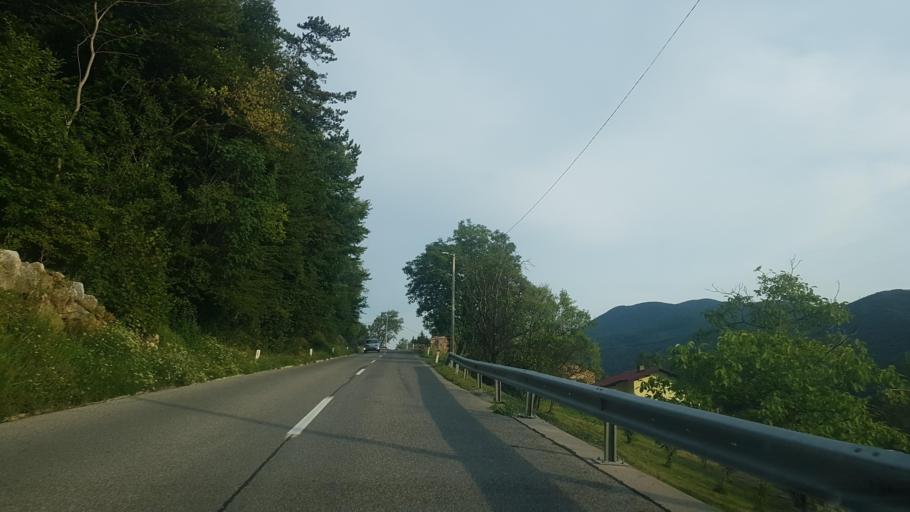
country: SI
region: Vipava
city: Vipava
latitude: 45.8778
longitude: 14.0082
